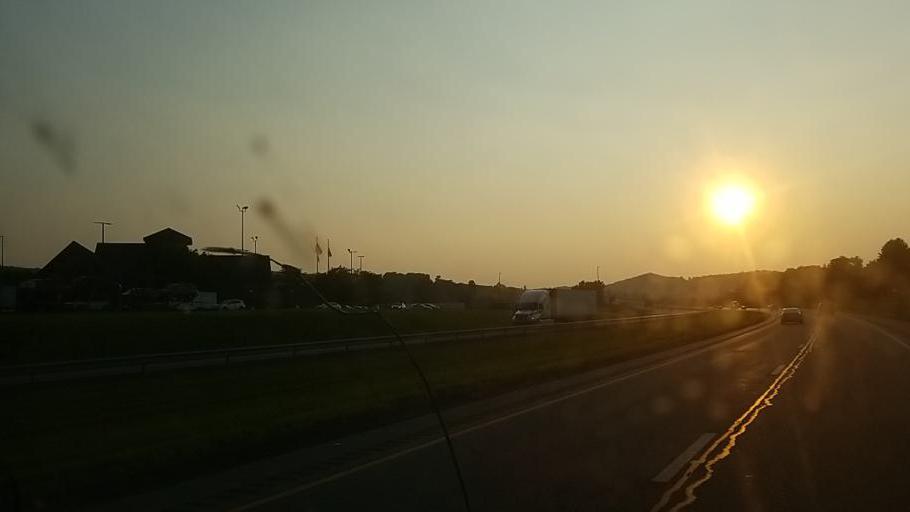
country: US
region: New York
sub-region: Herkimer County
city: Little Falls
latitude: 43.0165
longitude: -74.8023
